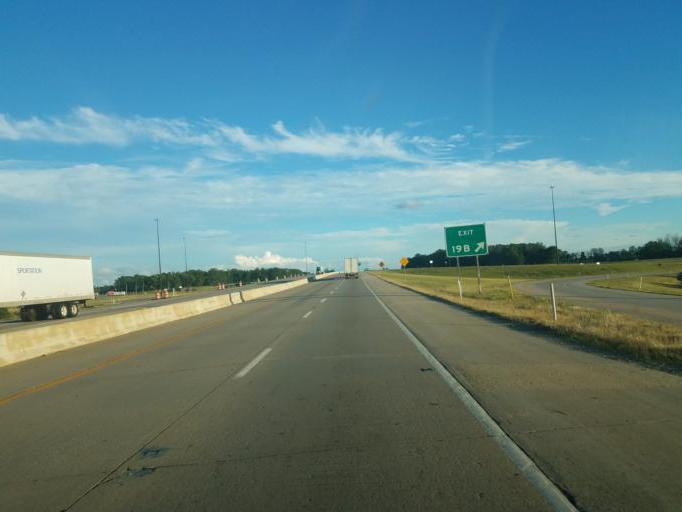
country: US
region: Indiana
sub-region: Allen County
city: New Haven
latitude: 41.0673
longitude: -84.9898
